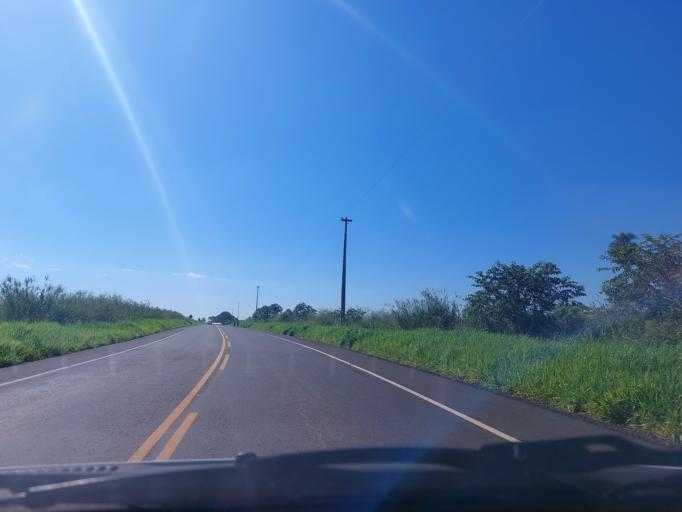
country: PY
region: San Pedro
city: Guayaybi
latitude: -24.3175
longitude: -56.1683
